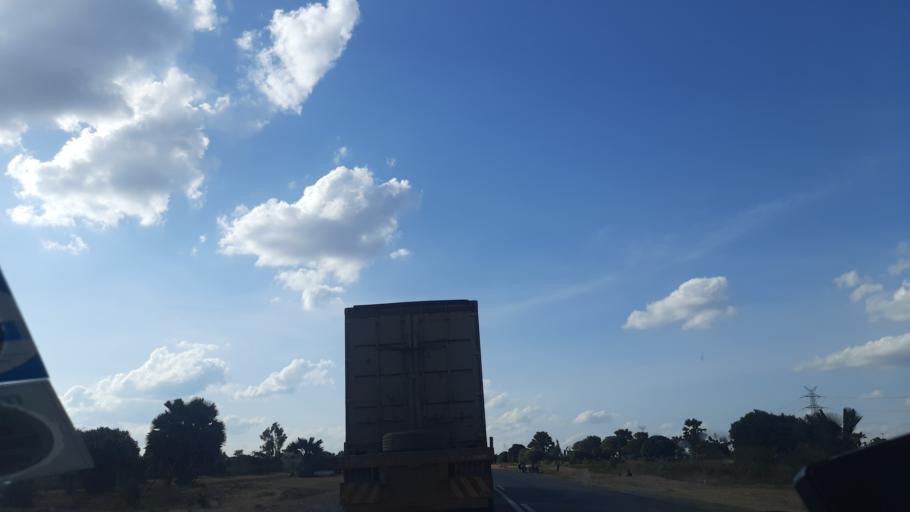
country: TZ
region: Singida
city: Ikungi
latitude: -5.0886
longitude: 34.7657
